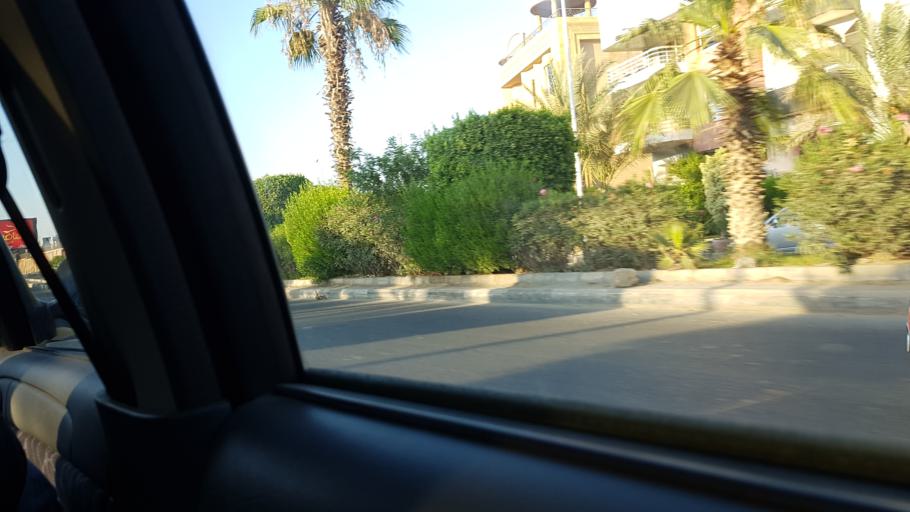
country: EG
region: Muhafazat al Qalyubiyah
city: Al Khankah
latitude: 30.0565
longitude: 31.4430
